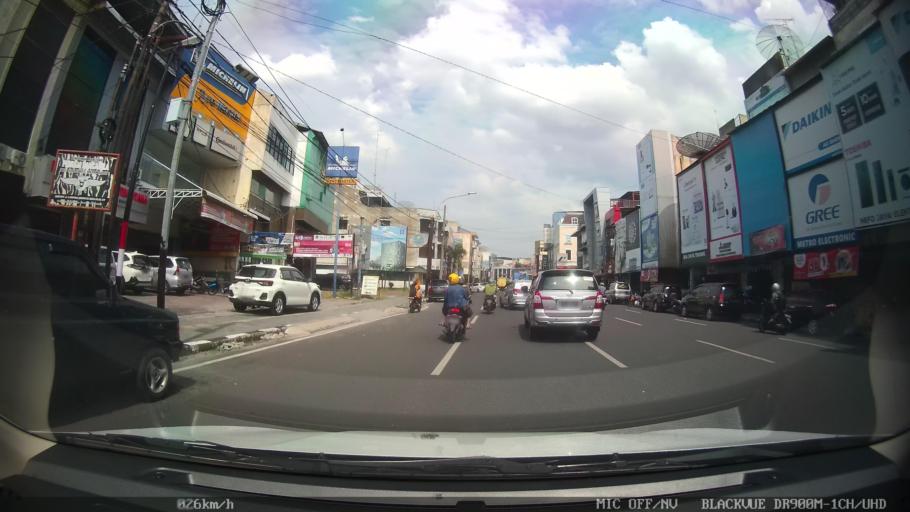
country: ID
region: North Sumatra
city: Medan
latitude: 3.5927
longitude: 98.6691
